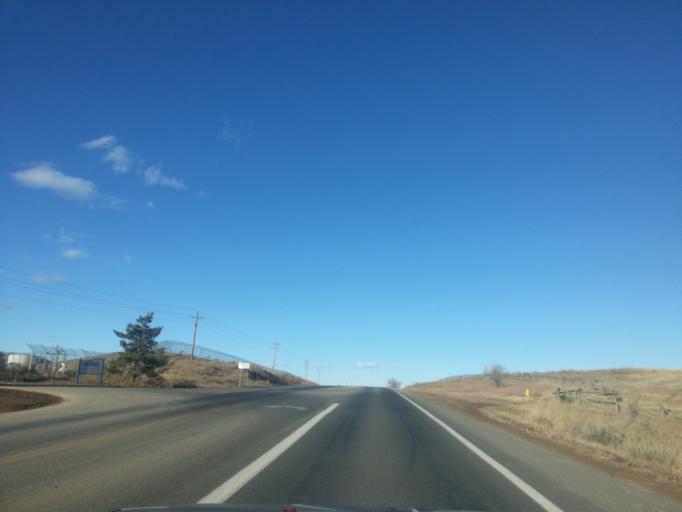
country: US
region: Colorado
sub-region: Larimer County
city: Fort Collins
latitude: 40.5044
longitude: -105.1153
